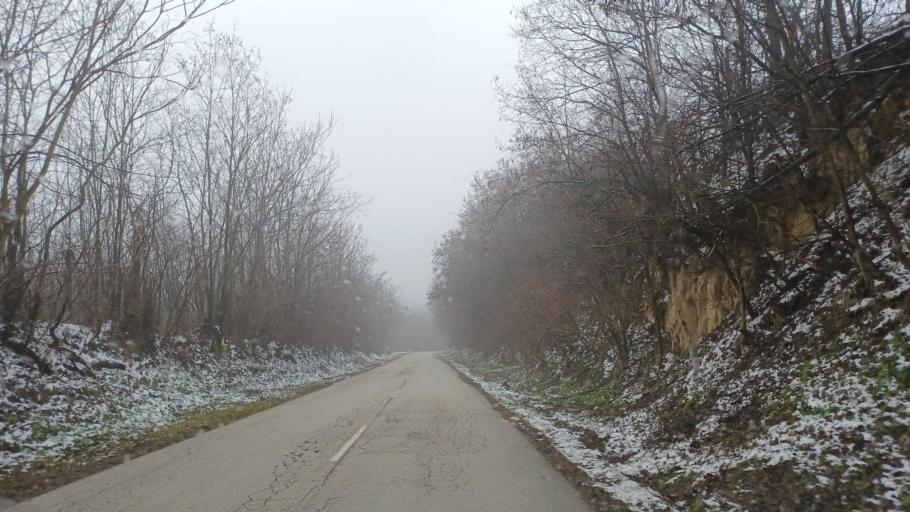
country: HU
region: Tolna
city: Gyonk
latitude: 46.6122
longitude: 18.4822
